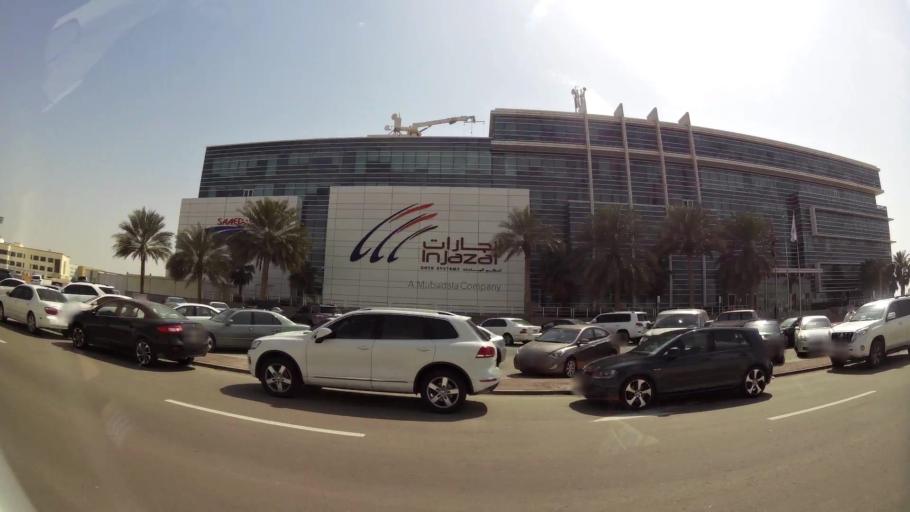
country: AE
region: Abu Dhabi
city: Abu Dhabi
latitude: 24.3185
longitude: 54.5552
